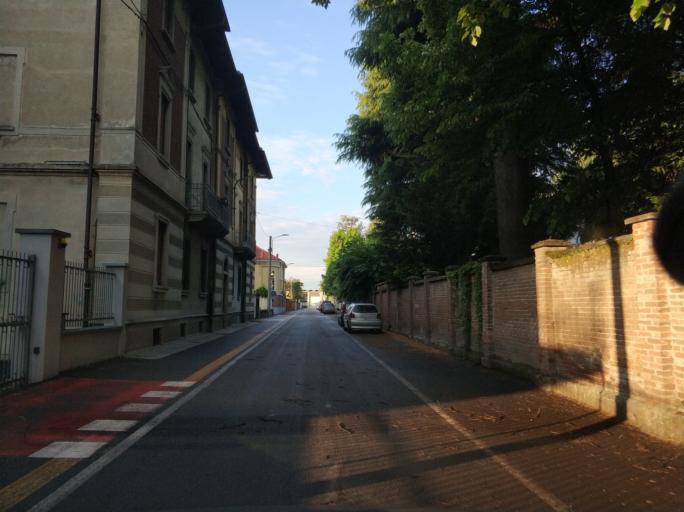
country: IT
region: Piedmont
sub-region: Provincia di Torino
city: Cirie
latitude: 45.2311
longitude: 7.6057
